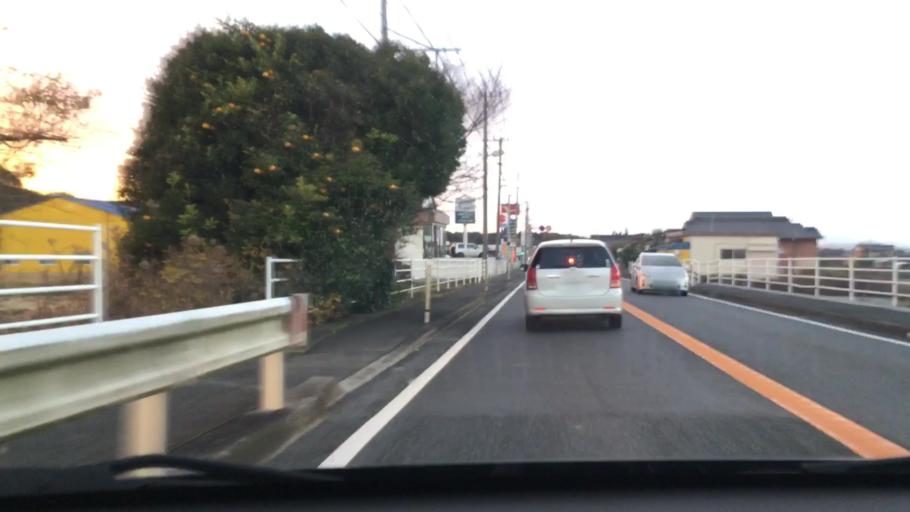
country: JP
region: Fukuoka
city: Shiida
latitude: 33.6319
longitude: 131.0814
